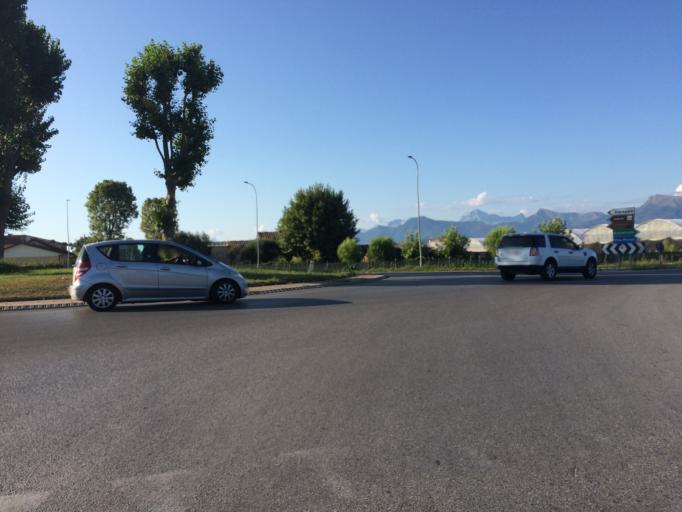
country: IT
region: Tuscany
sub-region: Provincia di Lucca
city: Torre del Lago Puccini
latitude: 43.8347
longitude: 10.2875
